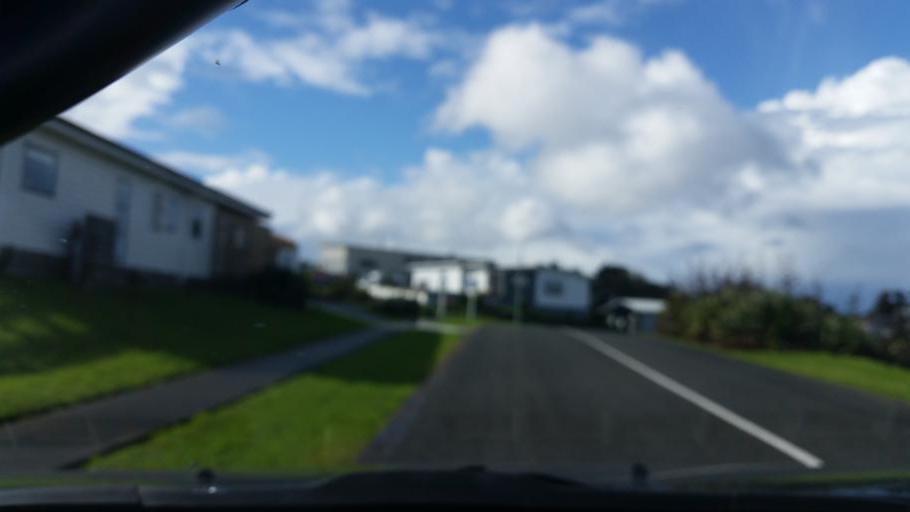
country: NZ
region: Auckland
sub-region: Auckland
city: Wellsford
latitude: -36.0872
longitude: 174.5778
